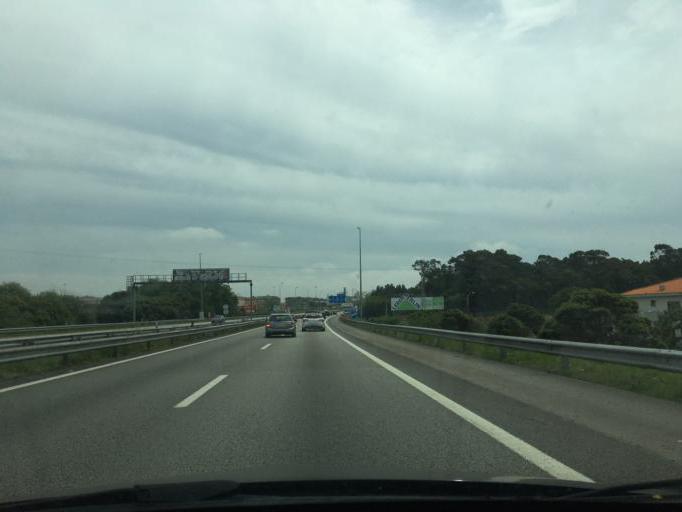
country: PT
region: Porto
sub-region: Matosinhos
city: Santa Cruz do Bispo
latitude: 41.2239
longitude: -8.6935
